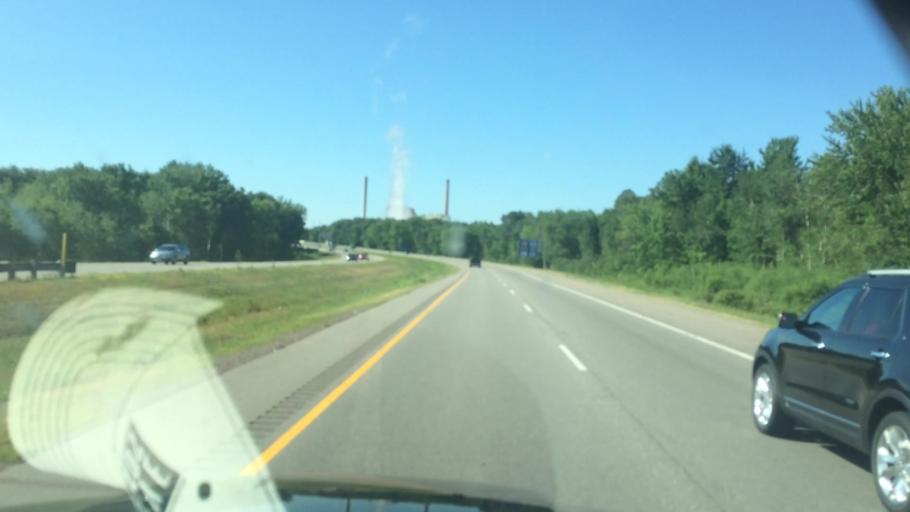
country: US
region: Wisconsin
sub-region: Marathon County
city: Rothschild
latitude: 44.8746
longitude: -89.6448
